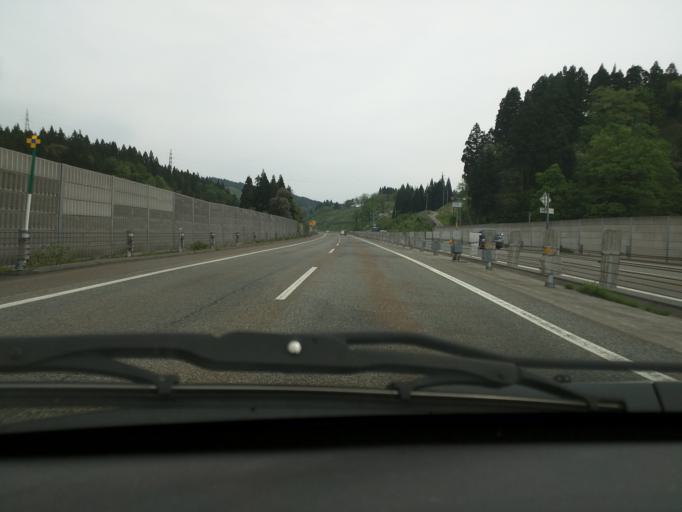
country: JP
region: Niigata
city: Ojiya
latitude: 37.2836
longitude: 138.7865
